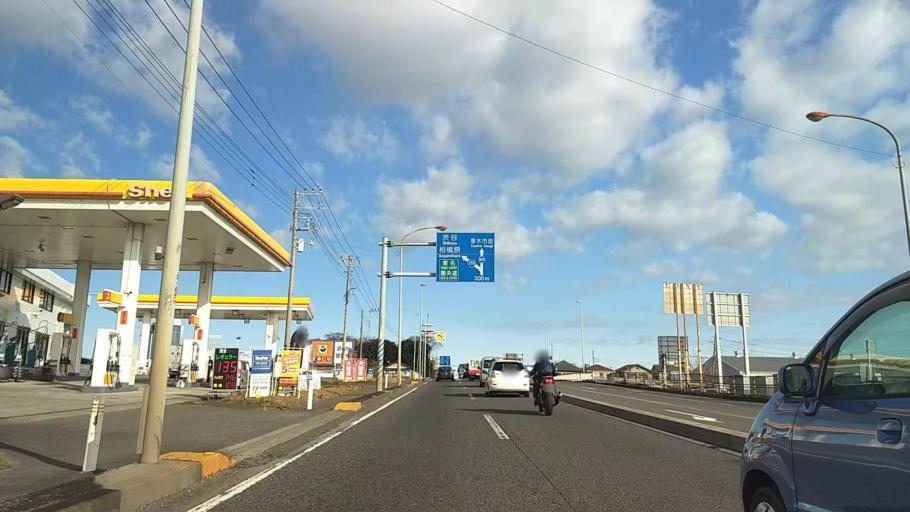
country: JP
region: Kanagawa
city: Atsugi
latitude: 35.4115
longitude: 139.3620
